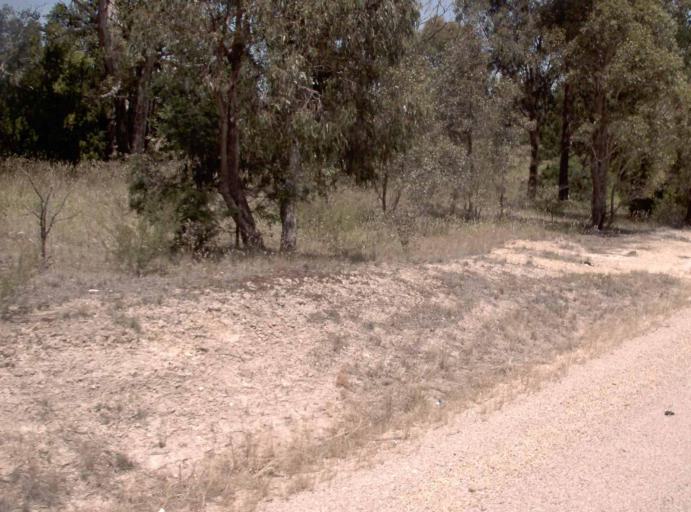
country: AU
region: Victoria
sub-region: East Gippsland
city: Bairnsdale
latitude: -37.7601
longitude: 147.7051
